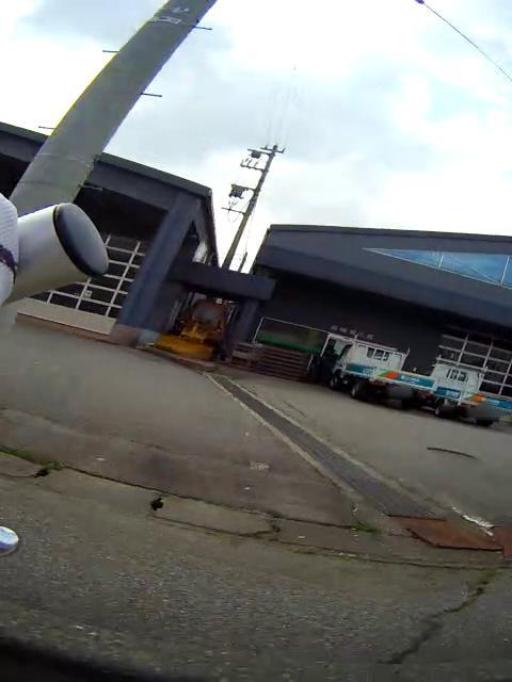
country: JP
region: Toyama
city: Takaoka
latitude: 36.7107
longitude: 136.9890
